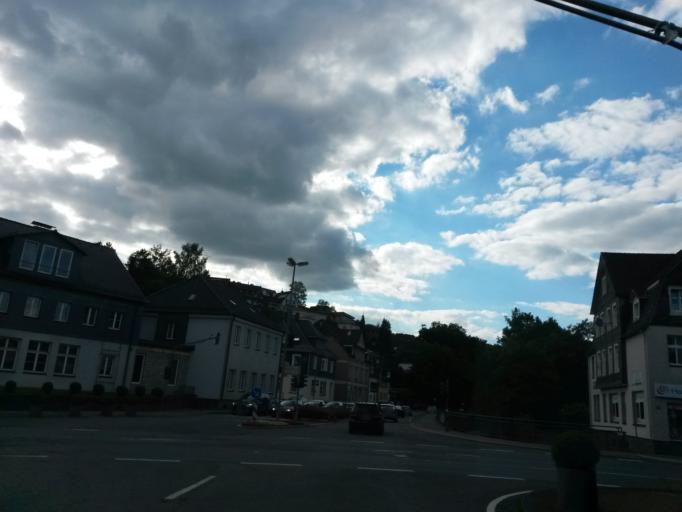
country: DE
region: North Rhine-Westphalia
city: Bergneustadt
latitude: 51.0080
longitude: 7.6246
